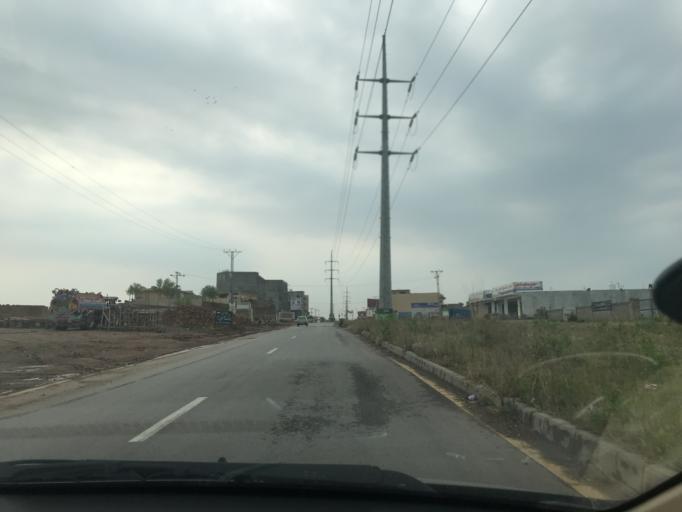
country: PK
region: Islamabad
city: Islamabad
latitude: 33.6869
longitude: 73.1660
